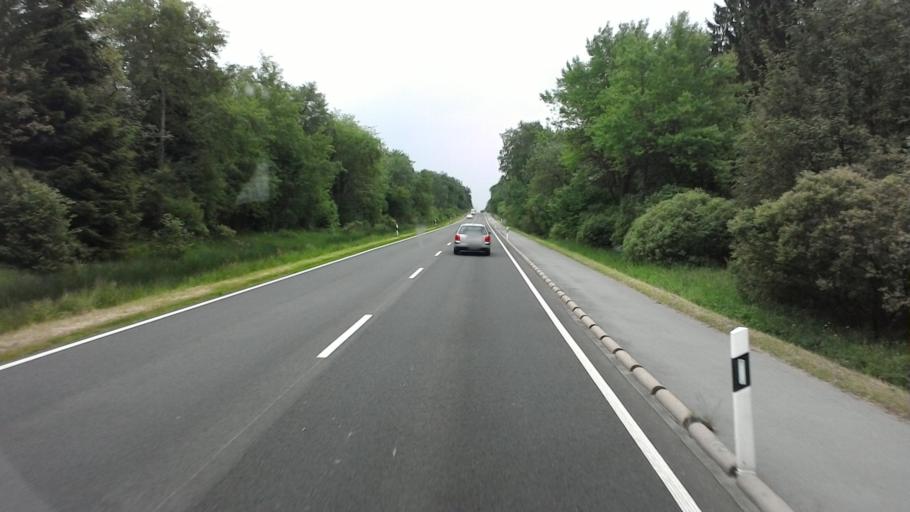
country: DE
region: North Rhine-Westphalia
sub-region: Regierungsbezirk Koln
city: Roetgen
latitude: 50.6167
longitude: 6.2407
